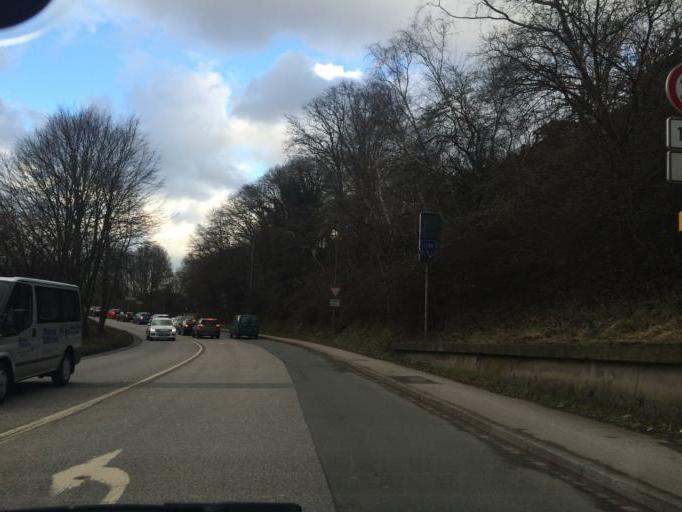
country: DE
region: North Rhine-Westphalia
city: Sprockhovel
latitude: 51.4139
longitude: 7.2678
